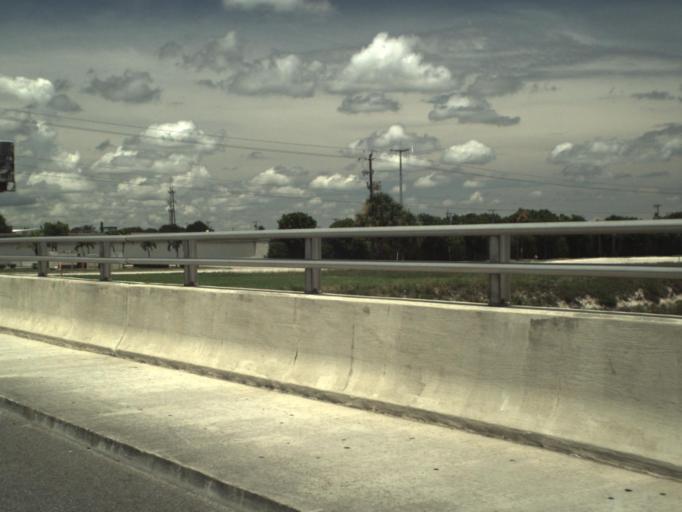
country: US
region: Florida
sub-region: Palm Beach County
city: Mangonia Park
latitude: 26.7831
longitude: -80.0913
